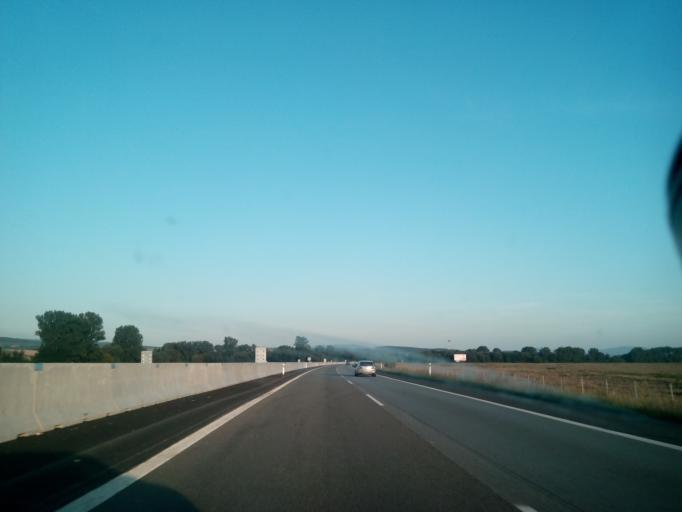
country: SK
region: Kosicky
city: Kosice
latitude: 48.8459
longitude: 21.2914
